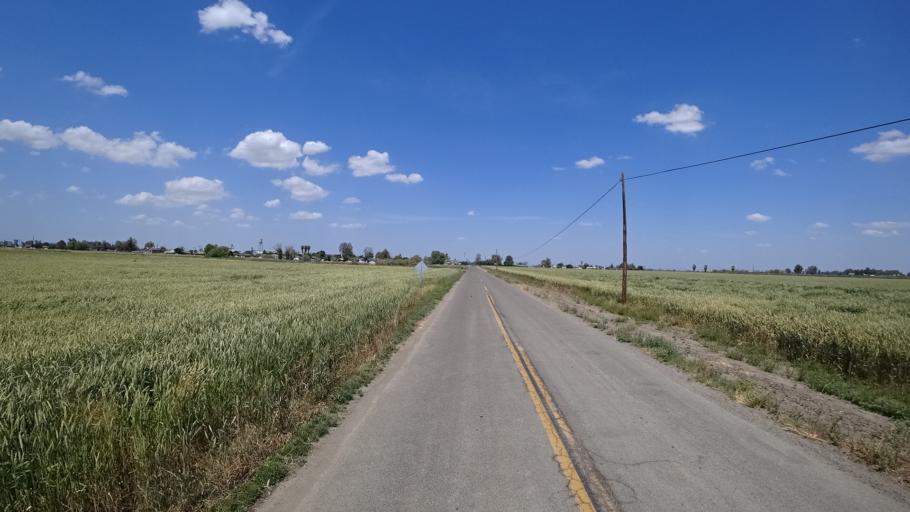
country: US
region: California
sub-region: Kings County
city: Stratford
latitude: 36.1829
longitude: -119.8206
